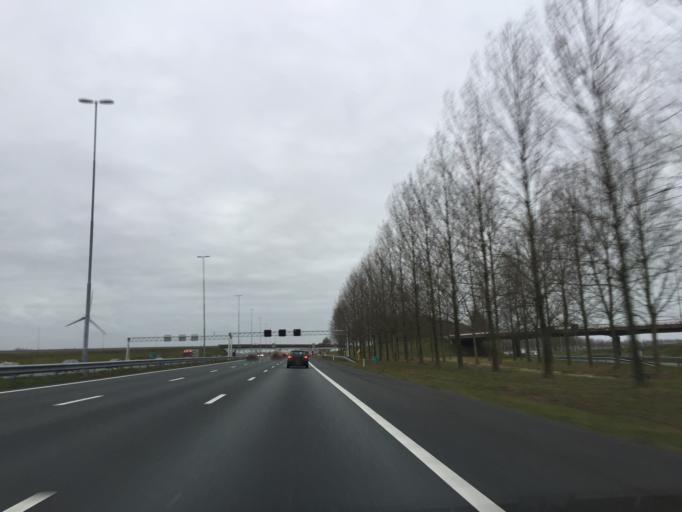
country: NL
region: South Holland
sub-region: Gemeente Kaag en Braassem
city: Leimuiden
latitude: 52.2360
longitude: 4.6518
